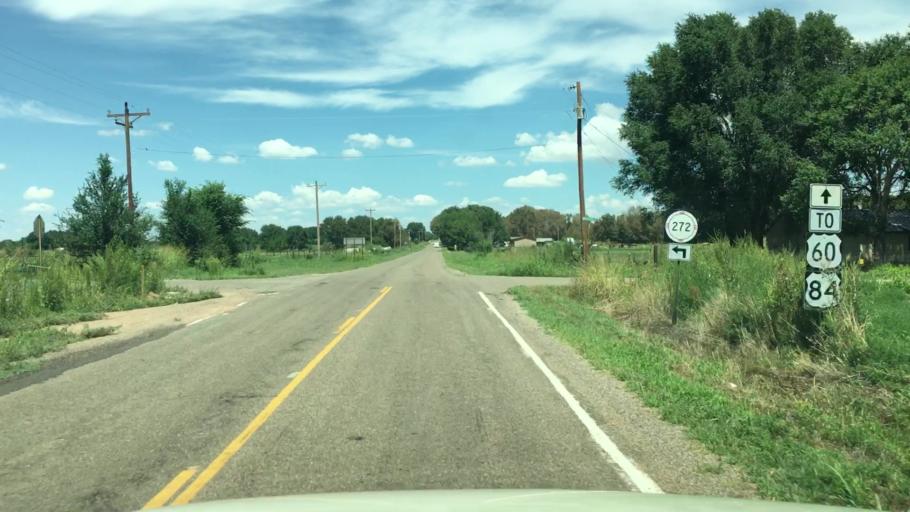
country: US
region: New Mexico
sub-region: De Baca County
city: Fort Sumner
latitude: 34.4340
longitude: -104.1935
